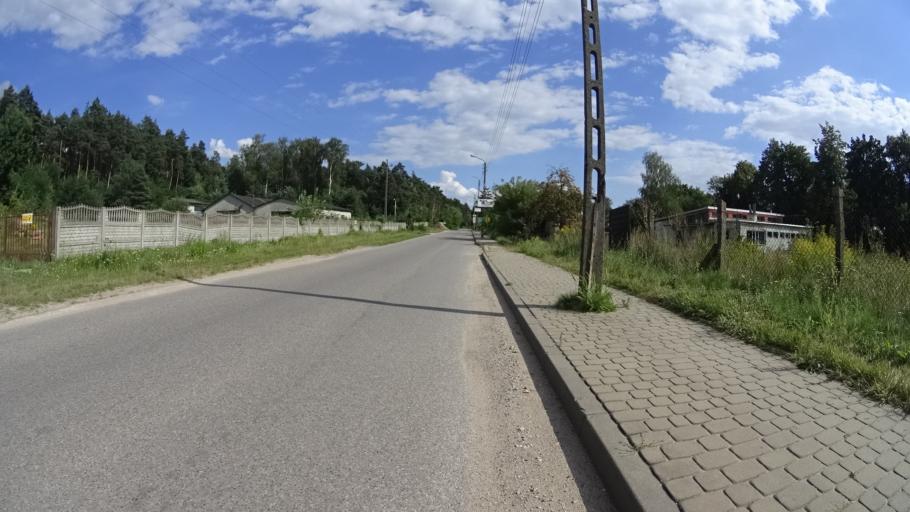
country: PL
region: Masovian Voivodeship
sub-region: Powiat grojecki
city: Mogielnica
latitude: 51.6957
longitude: 20.7285
